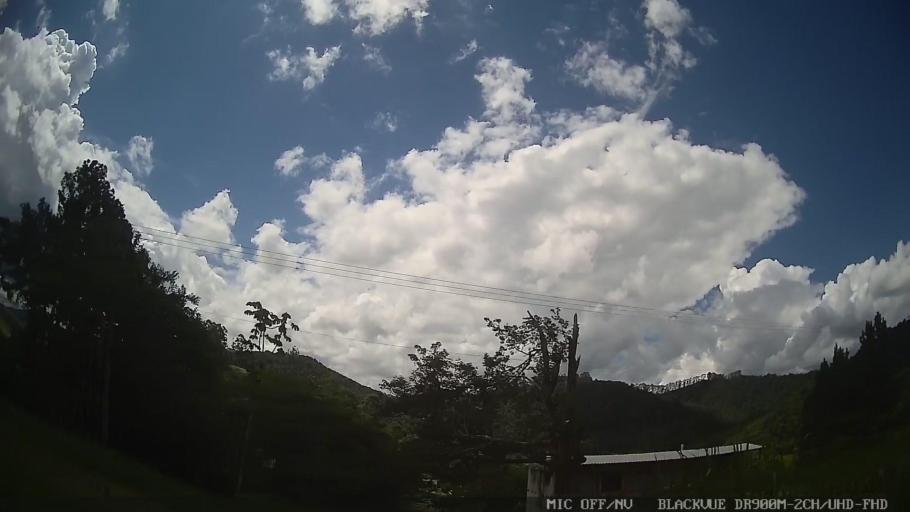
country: BR
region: Sao Paulo
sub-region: Caraguatatuba
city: Caraguatatuba
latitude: -23.5356
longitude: -45.5703
